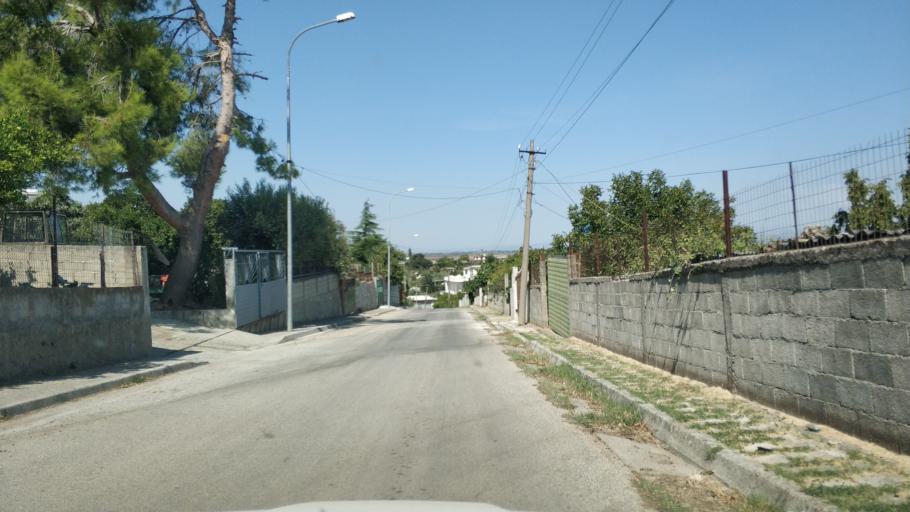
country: AL
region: Fier
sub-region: Rrethi i Lushnjes
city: Kolonje
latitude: 40.8251
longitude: 19.6029
